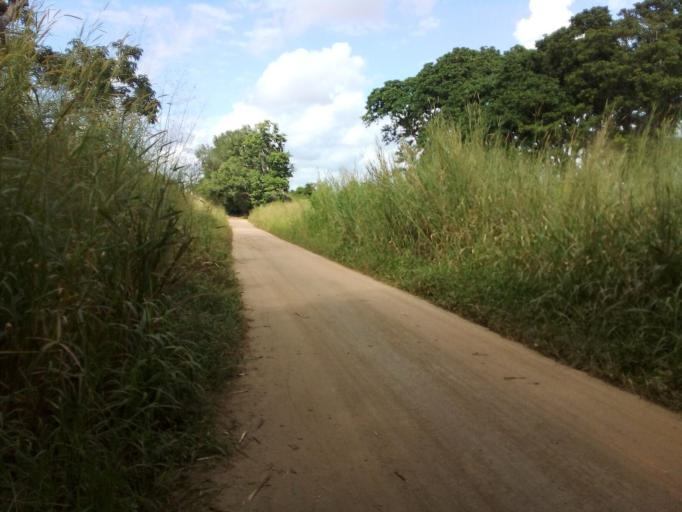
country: MZ
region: Zambezia
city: Quelimane
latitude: -17.5501
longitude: 36.6952
